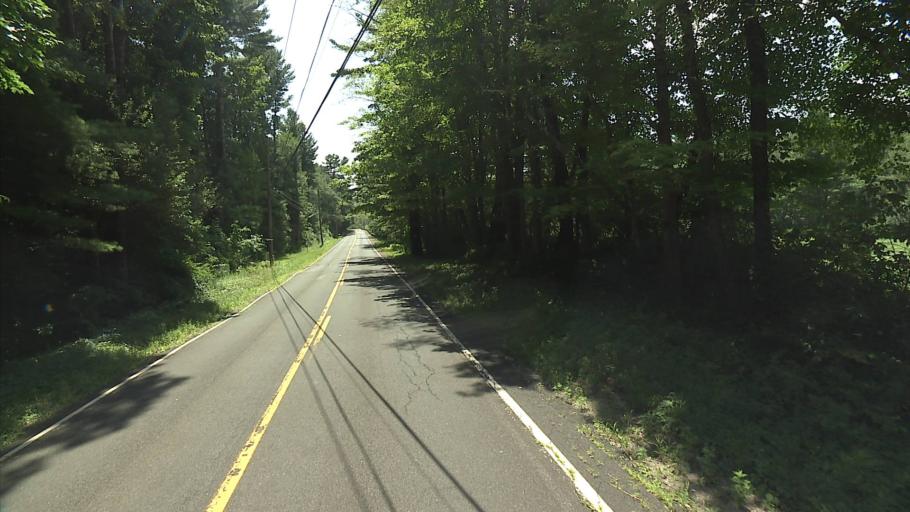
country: US
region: Connecticut
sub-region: Litchfield County
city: Canaan
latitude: 41.8793
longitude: -73.2894
